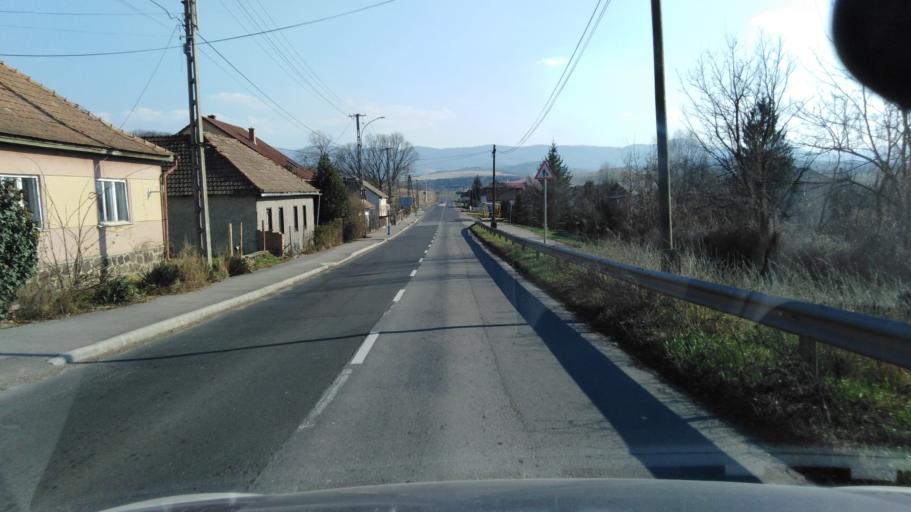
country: HU
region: Nograd
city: Batonyterenye
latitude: 48.0061
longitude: 19.8480
